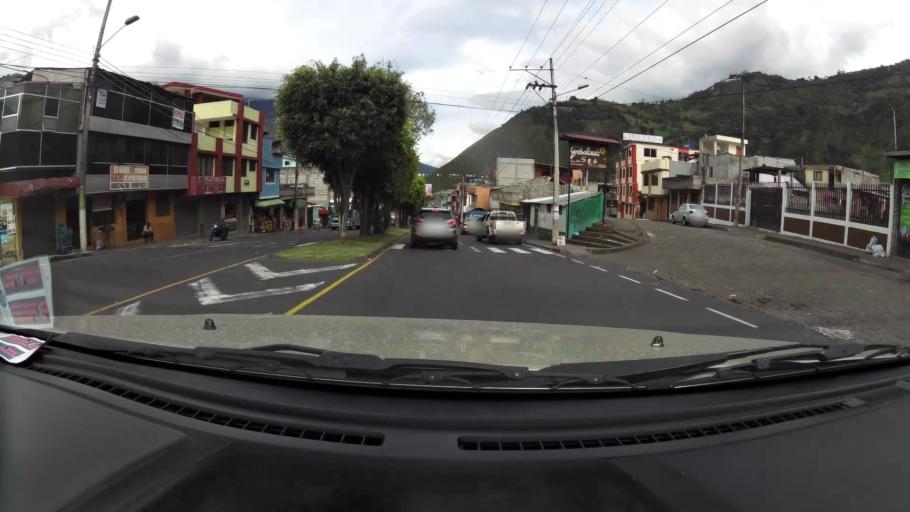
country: EC
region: Tungurahua
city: Banos
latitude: -1.3949
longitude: -78.4261
